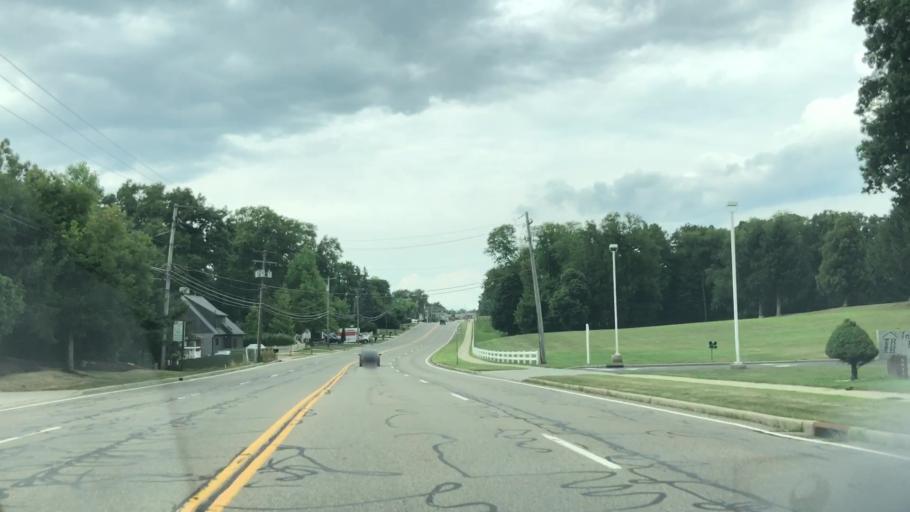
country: US
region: Ohio
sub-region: Summit County
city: Portage Lakes
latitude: 40.9933
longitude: -81.5225
